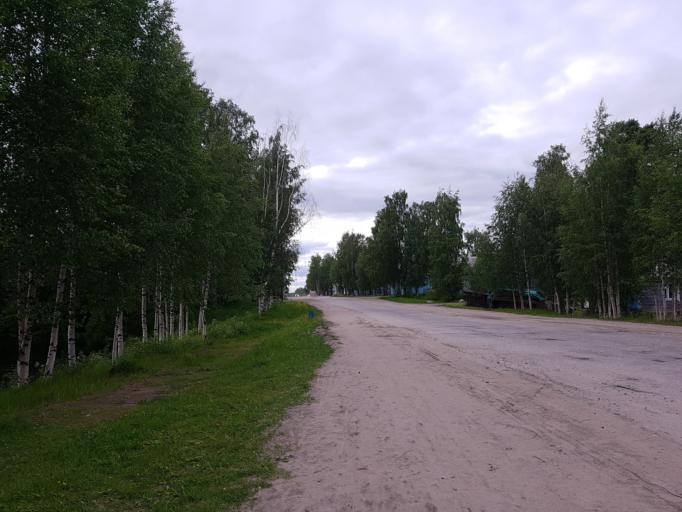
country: RU
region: Republic of Karelia
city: Kalevala
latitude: 65.1953
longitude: 31.1830
